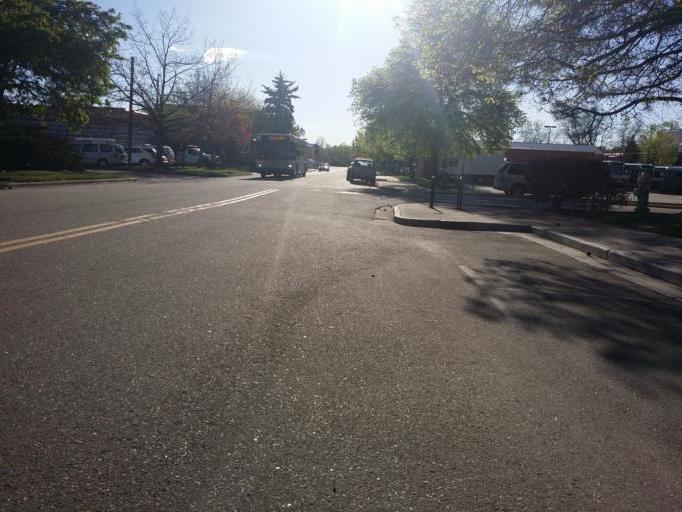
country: US
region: Colorado
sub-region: Boulder County
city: Boulder
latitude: 40.0135
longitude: -105.2518
